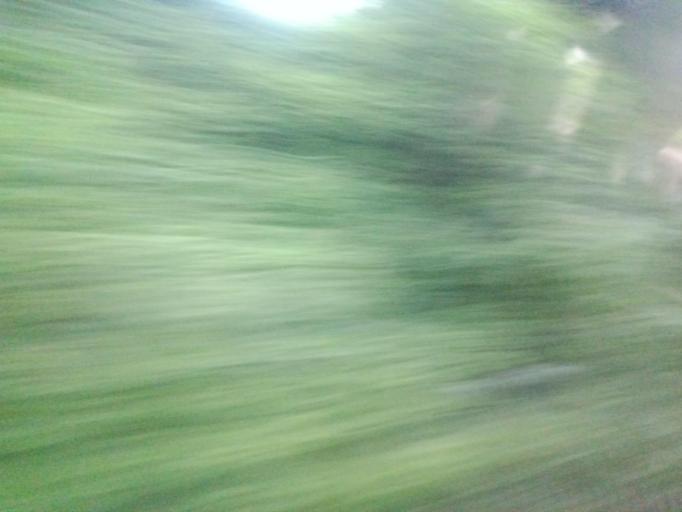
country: IE
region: Leinster
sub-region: Laois
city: Mountmellick
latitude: 53.1117
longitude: -7.3569
